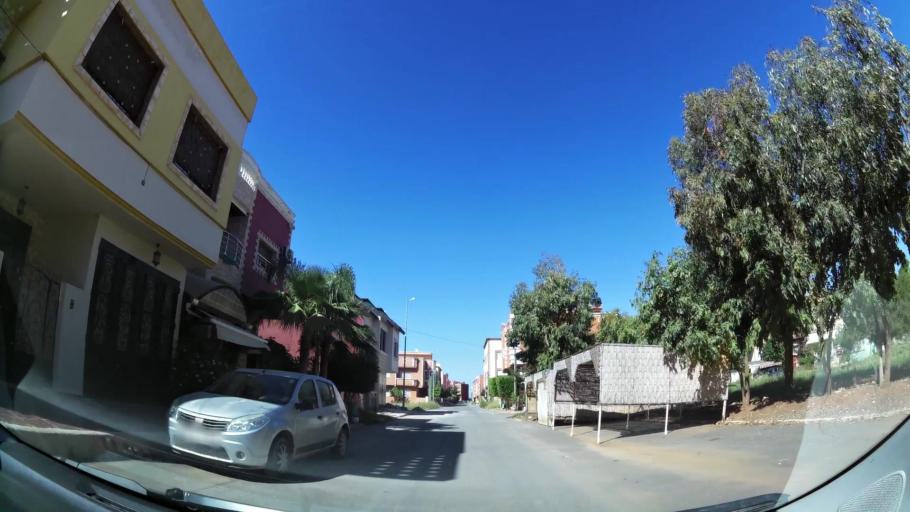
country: MA
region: Oriental
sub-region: Berkane-Taourirt
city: Berkane
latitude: 34.9445
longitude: -2.3374
